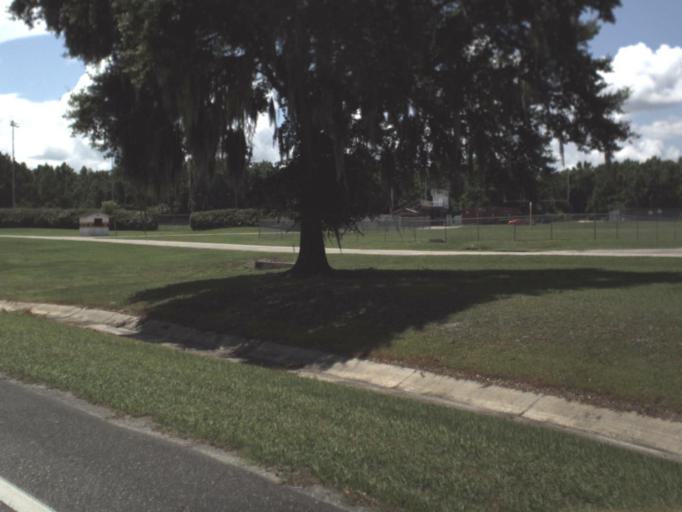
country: US
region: Florida
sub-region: Putnam County
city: Crescent City
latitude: 29.4731
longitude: -81.5340
